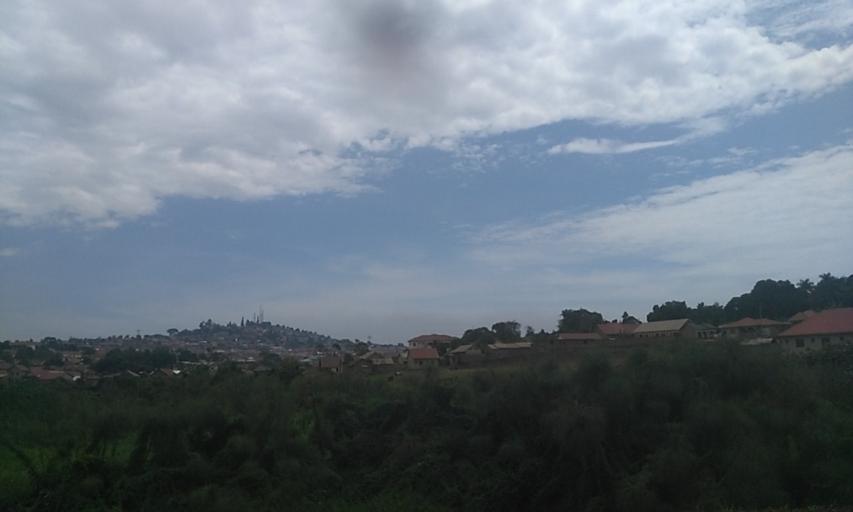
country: UG
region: Central Region
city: Kampala Central Division
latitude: 0.3386
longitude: 32.5323
